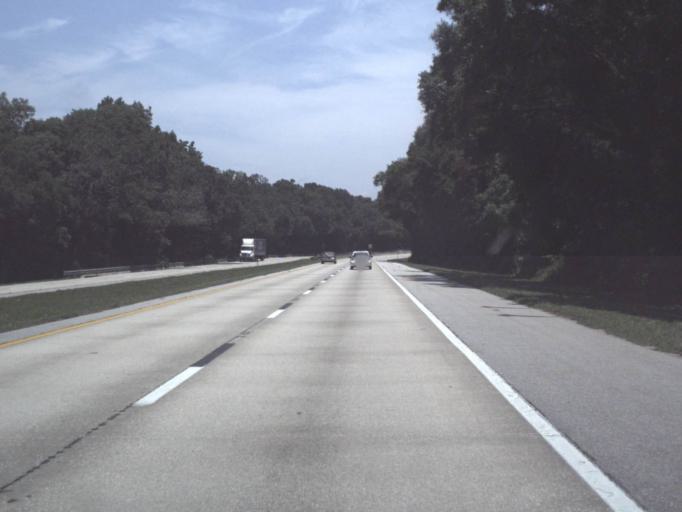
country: US
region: Florida
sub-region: Duval County
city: Jacksonville
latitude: 30.2922
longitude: -81.5891
